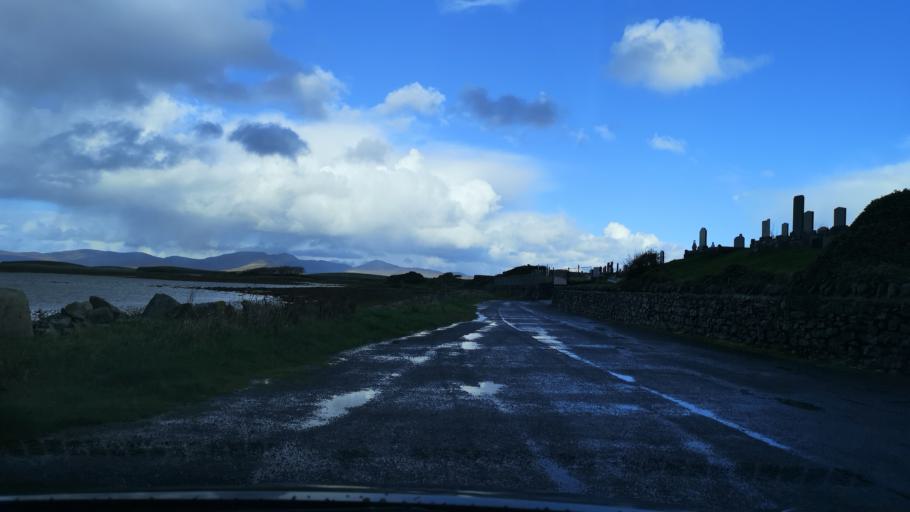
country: IE
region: Connaught
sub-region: Maigh Eo
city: Westport
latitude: 53.7823
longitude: -9.6402
